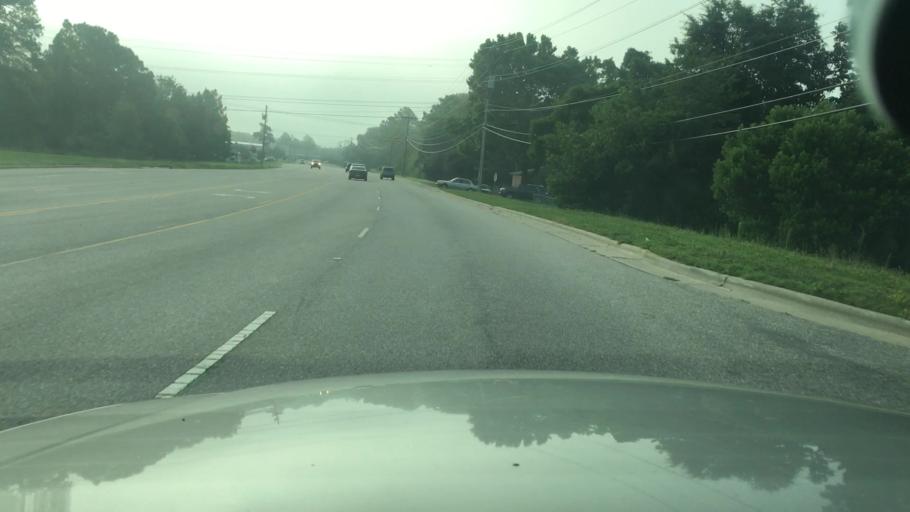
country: US
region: North Carolina
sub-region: Cumberland County
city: Hope Mills
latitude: 35.0026
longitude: -78.9143
